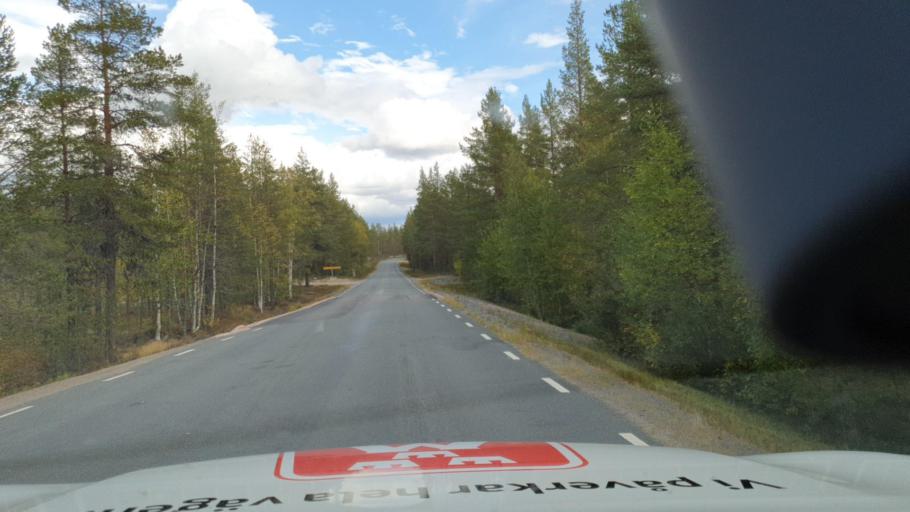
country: SE
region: Dalarna
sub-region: Alvdalens Kommun
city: AElvdalen
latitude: 61.6844
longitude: 13.2408
